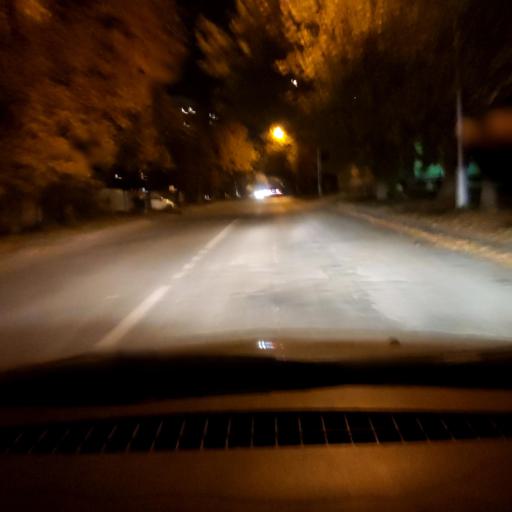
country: RU
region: Bashkortostan
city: Ufa
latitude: 54.7212
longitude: 55.9608
